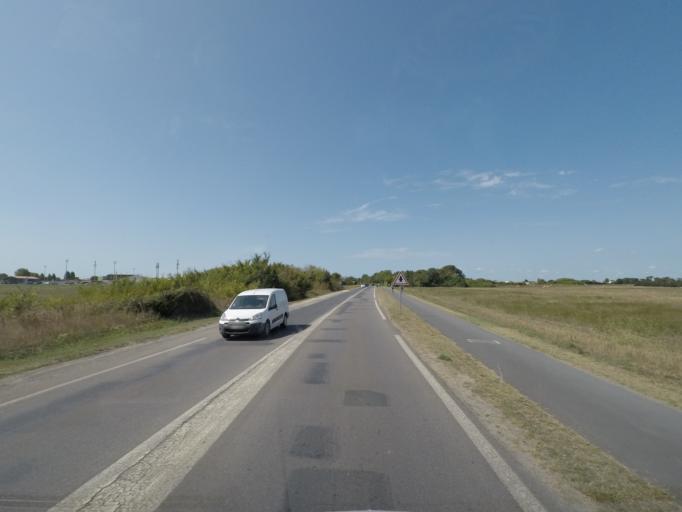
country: FR
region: Poitou-Charentes
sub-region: Departement de la Charente-Maritime
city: La Flotte
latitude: 46.1946
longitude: -1.3477
